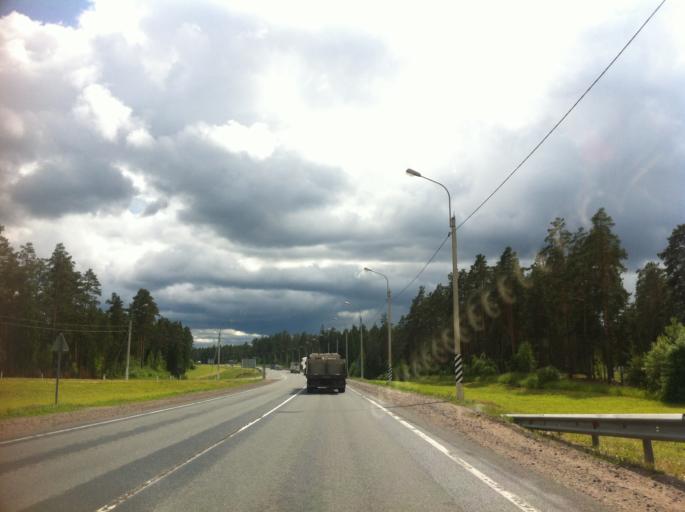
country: RU
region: Leningrad
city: Luga
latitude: 58.7269
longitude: 29.8797
